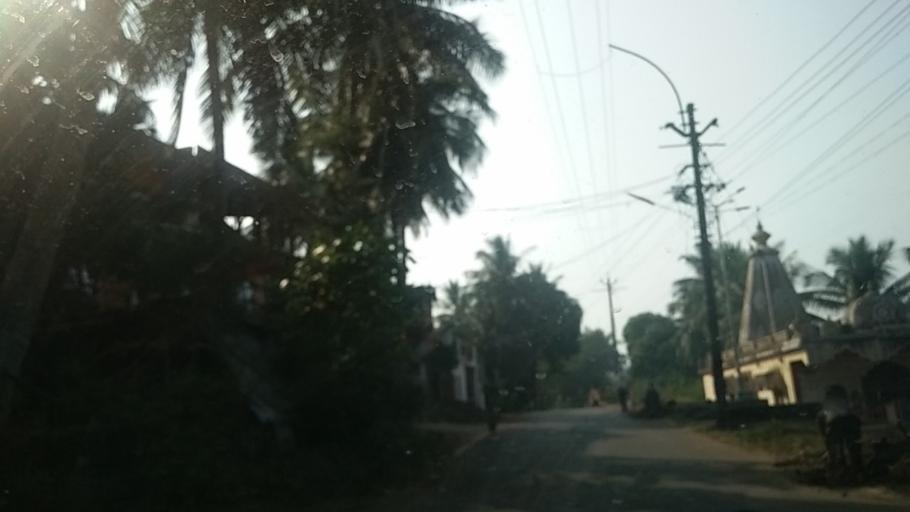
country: IN
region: Goa
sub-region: North Goa
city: Pernem
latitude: 15.7265
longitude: 73.7799
